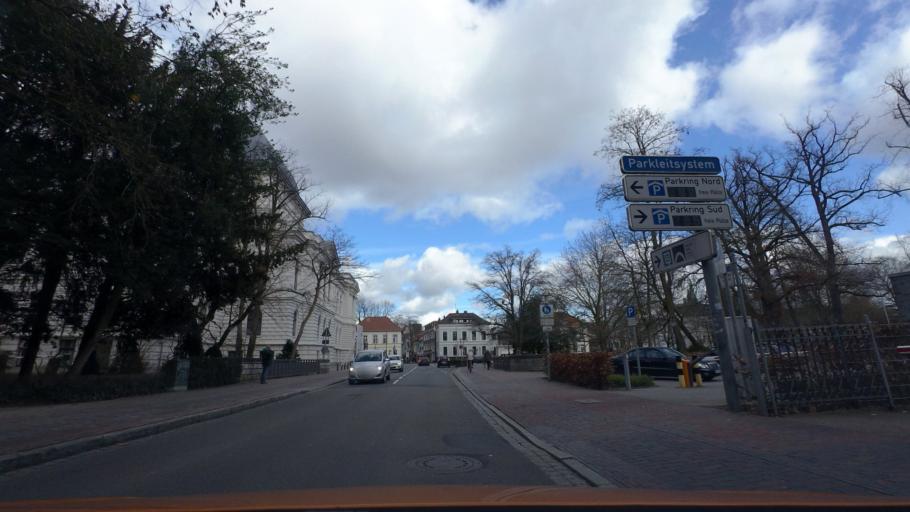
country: DE
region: Lower Saxony
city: Oldenburg
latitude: 53.1385
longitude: 8.2102
